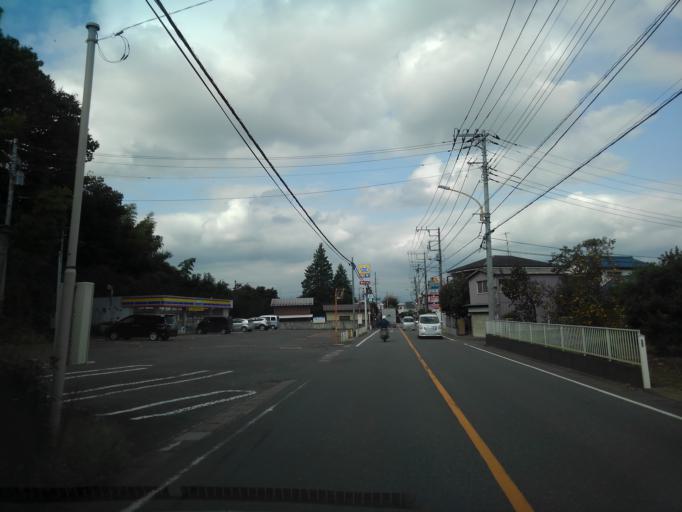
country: JP
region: Saitama
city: Sayama
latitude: 35.7908
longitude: 139.3898
